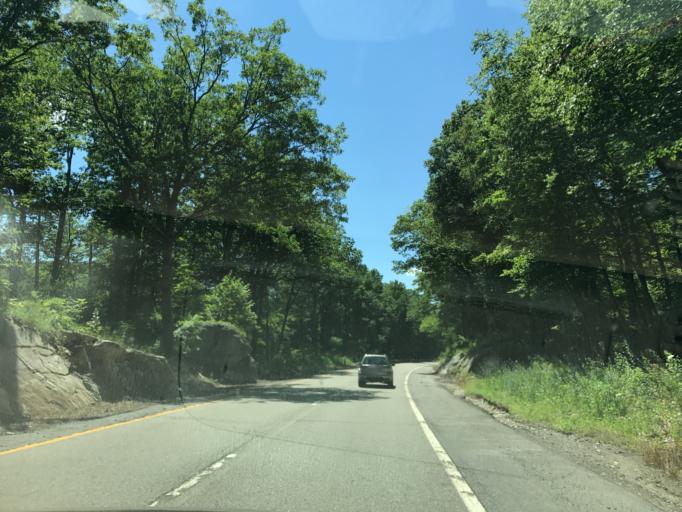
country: US
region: New York
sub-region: Dutchess County
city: Brinckerhoff
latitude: 41.4511
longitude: -73.8176
